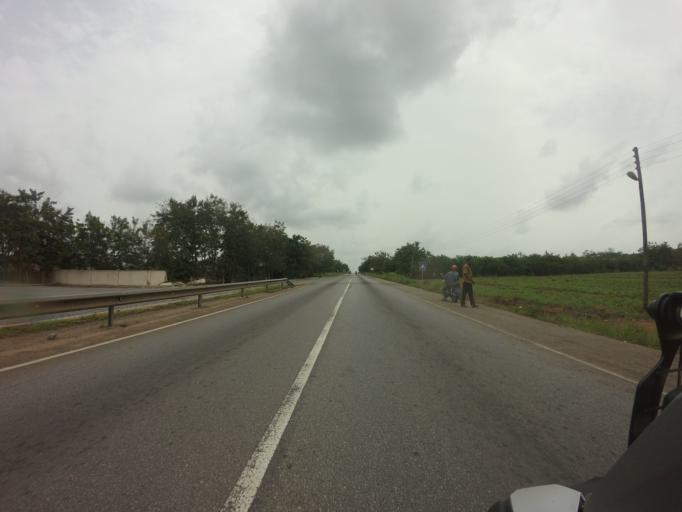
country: GH
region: Volta
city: Keta
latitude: 6.0995
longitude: 0.7643
